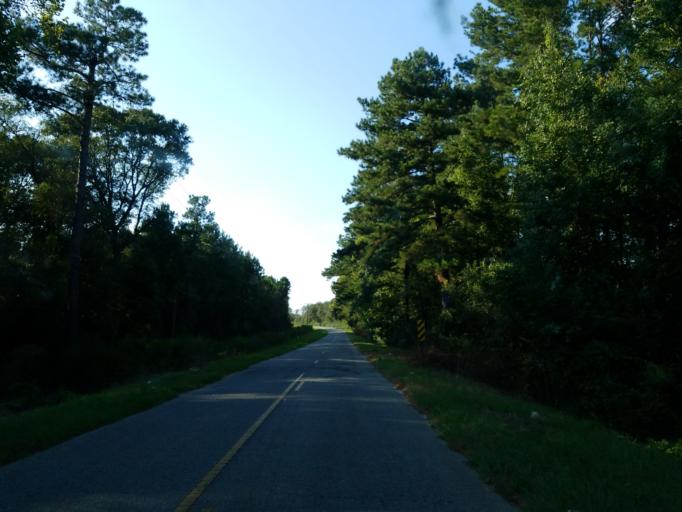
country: US
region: Georgia
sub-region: Cook County
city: Sparks
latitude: 31.2301
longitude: -83.4877
